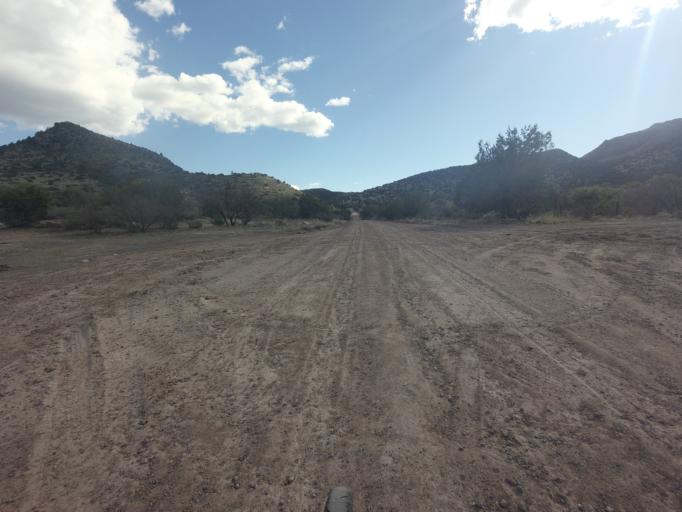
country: US
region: Arizona
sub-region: Yavapai County
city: Camp Verde
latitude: 34.4349
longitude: -111.6872
